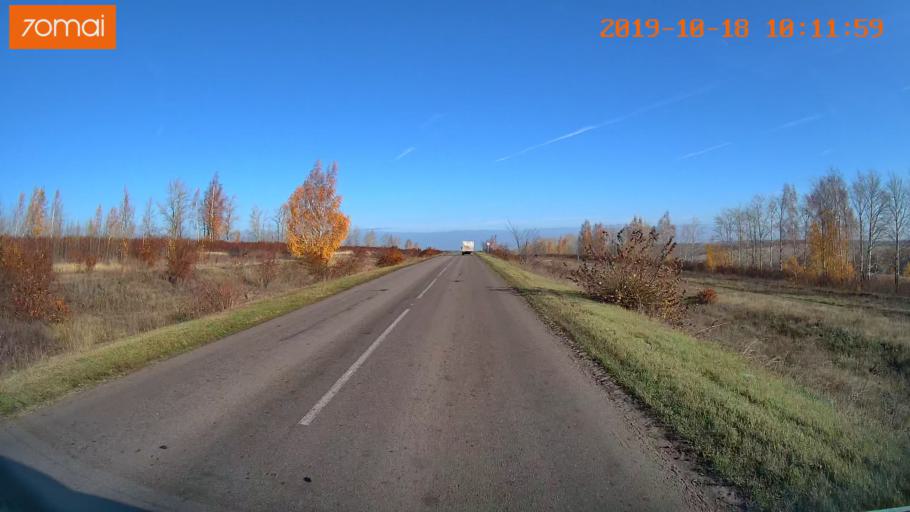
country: RU
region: Tula
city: Kurkino
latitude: 53.3886
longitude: 38.5042
